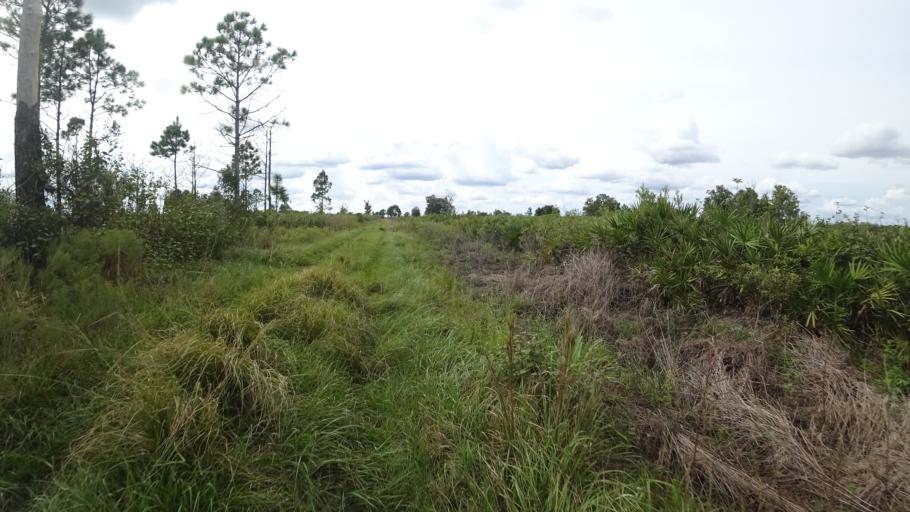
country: US
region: Florida
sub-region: Hillsborough County
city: Wimauma
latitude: 27.5594
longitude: -82.1207
